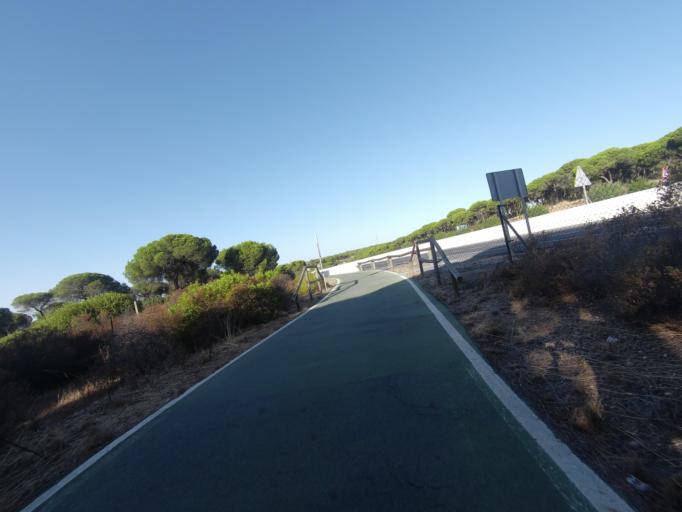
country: ES
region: Andalusia
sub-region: Provincia de Huelva
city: Aljaraque
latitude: 37.2282
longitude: -7.0213
